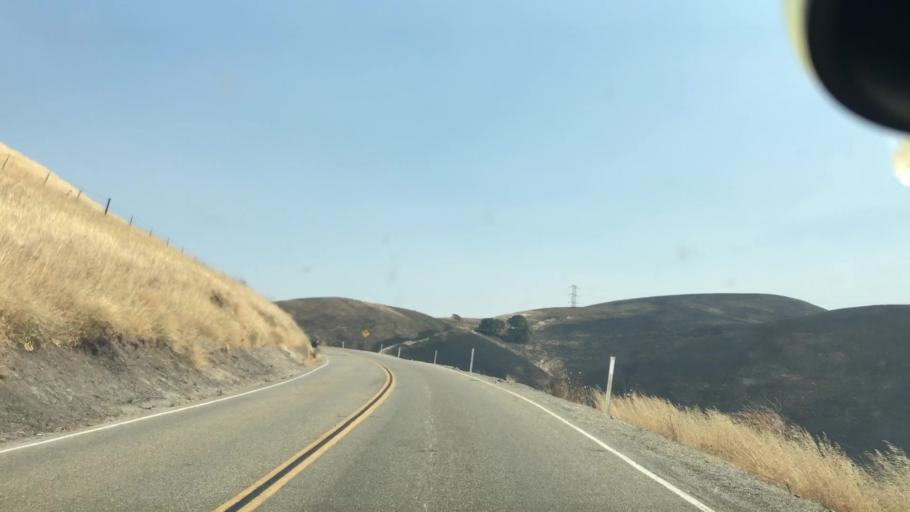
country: US
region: California
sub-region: San Joaquin County
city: Mountain House
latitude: 37.6508
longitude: -121.6130
